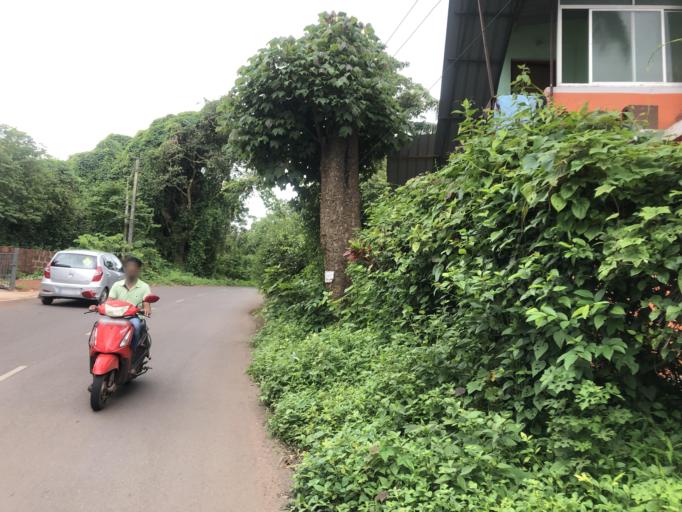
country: IN
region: Goa
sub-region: North Goa
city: Serula
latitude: 15.5402
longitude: 73.8317
